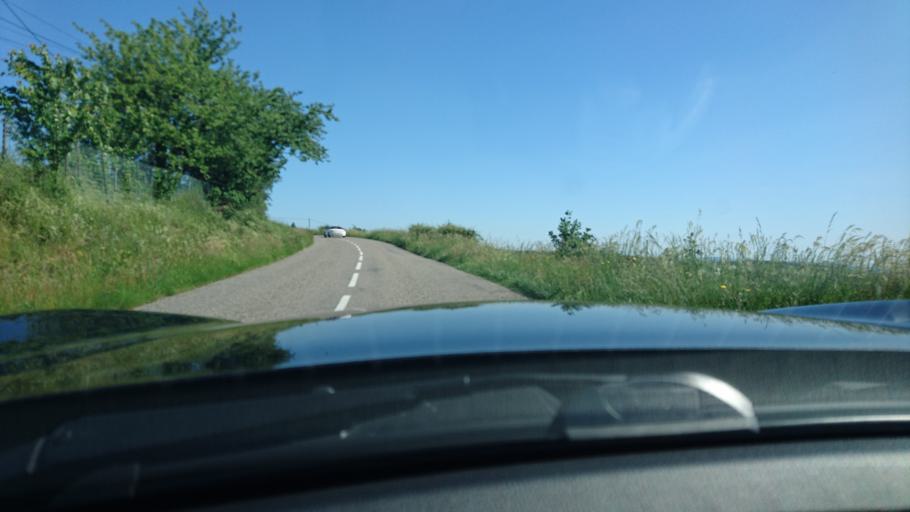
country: FR
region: Rhone-Alpes
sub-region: Departement du Rhone
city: Bessenay
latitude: 45.7824
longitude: 4.5459
